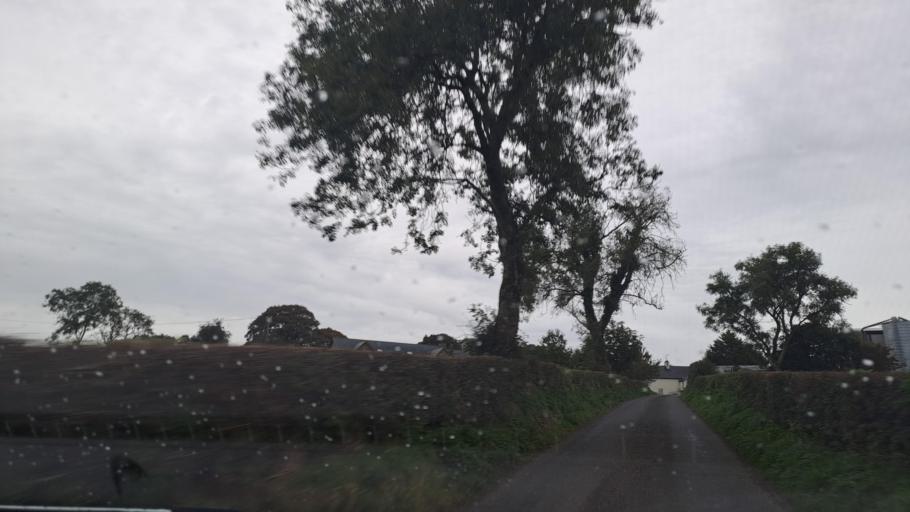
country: IE
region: Ulster
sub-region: An Cabhan
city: Kingscourt
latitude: 53.9970
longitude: -6.8111
